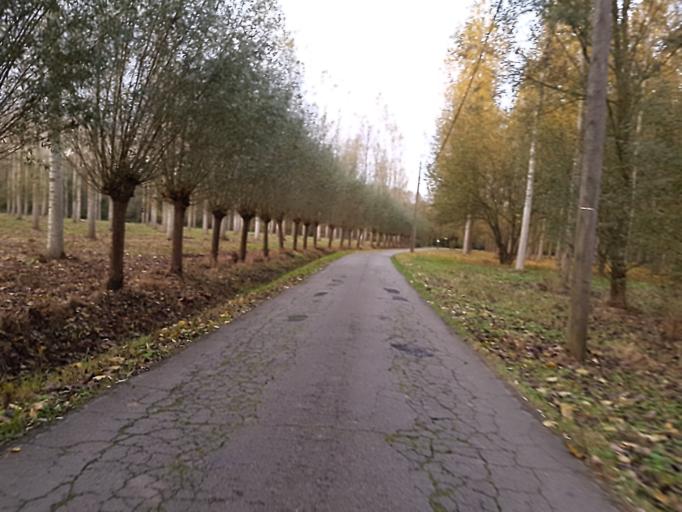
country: BE
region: Flanders
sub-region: Provincie Antwerpen
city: Ranst
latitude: 51.1956
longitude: 4.5723
